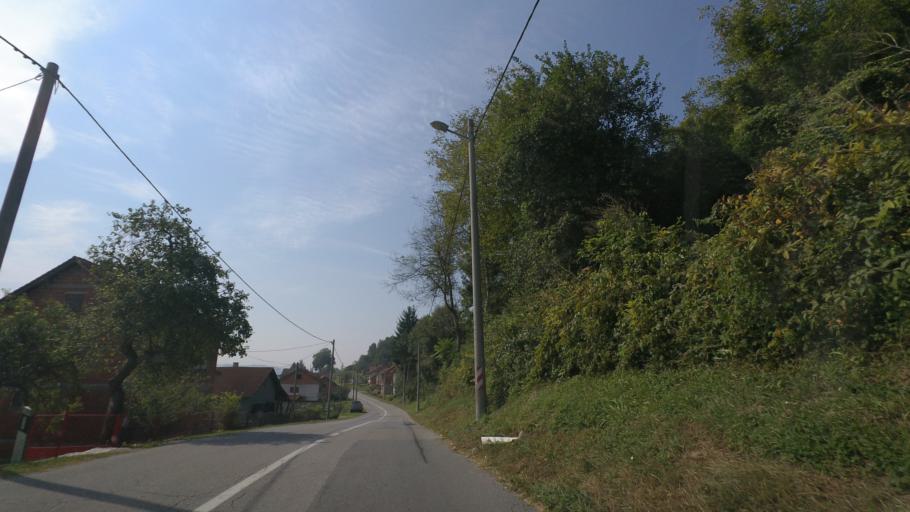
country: HR
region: Sisacko-Moslavacka
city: Dvor
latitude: 45.1040
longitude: 16.3885
